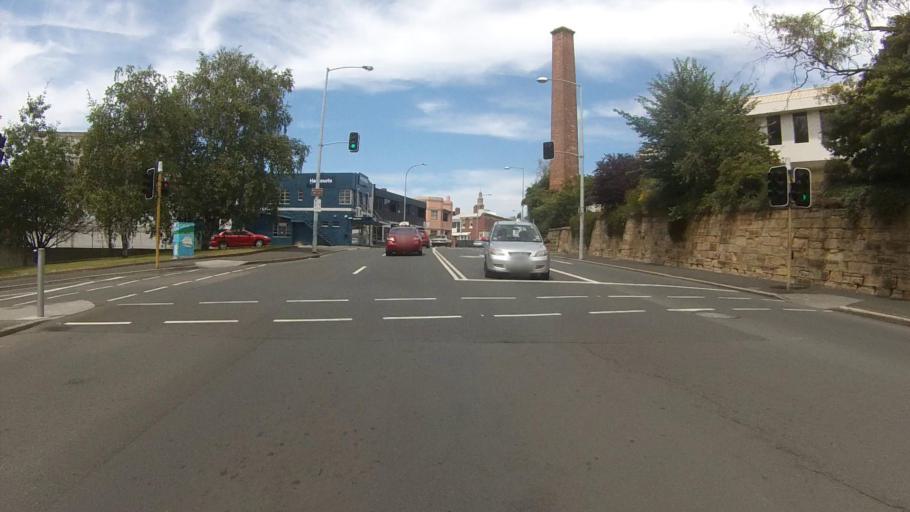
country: AU
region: Tasmania
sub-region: Hobart
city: Sandy Bay
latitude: -42.8878
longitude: 147.3296
